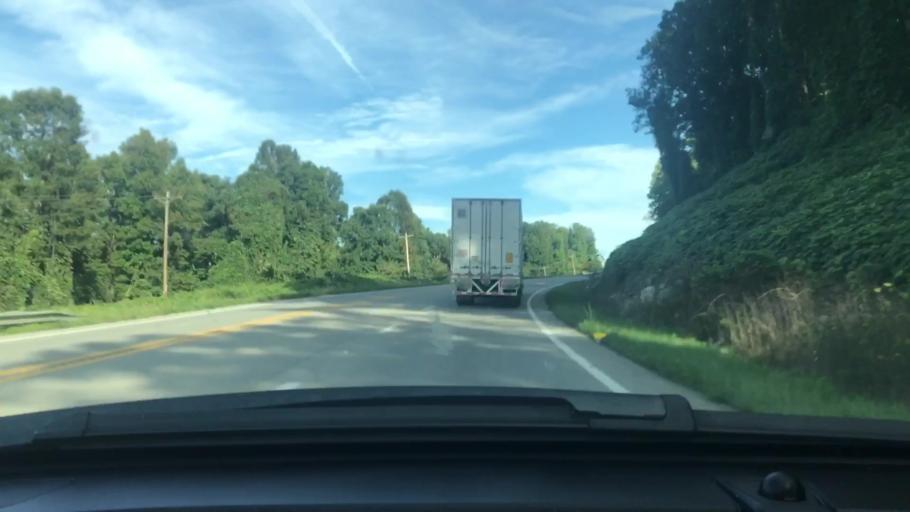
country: US
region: Arkansas
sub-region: Sharp County
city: Cherokee Village
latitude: 36.3003
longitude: -91.4076
